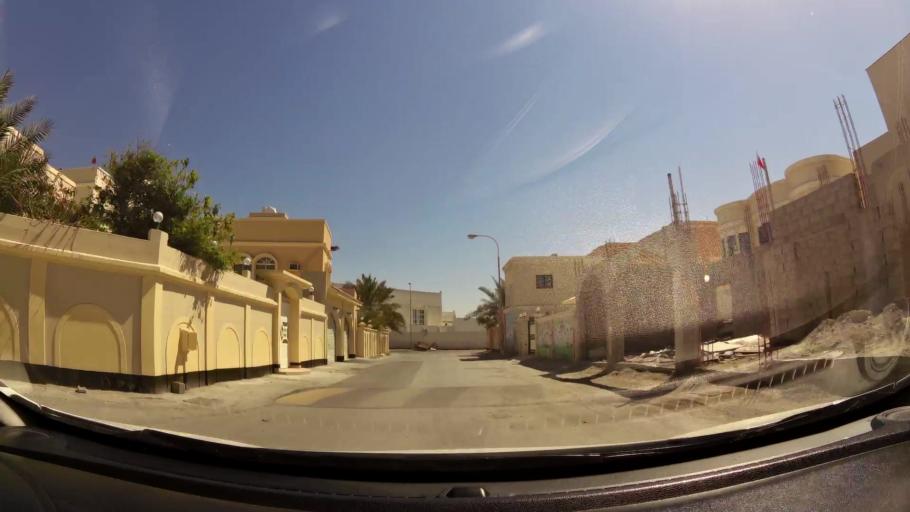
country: BH
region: Muharraq
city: Al Muharraq
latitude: 26.2771
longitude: 50.6378
